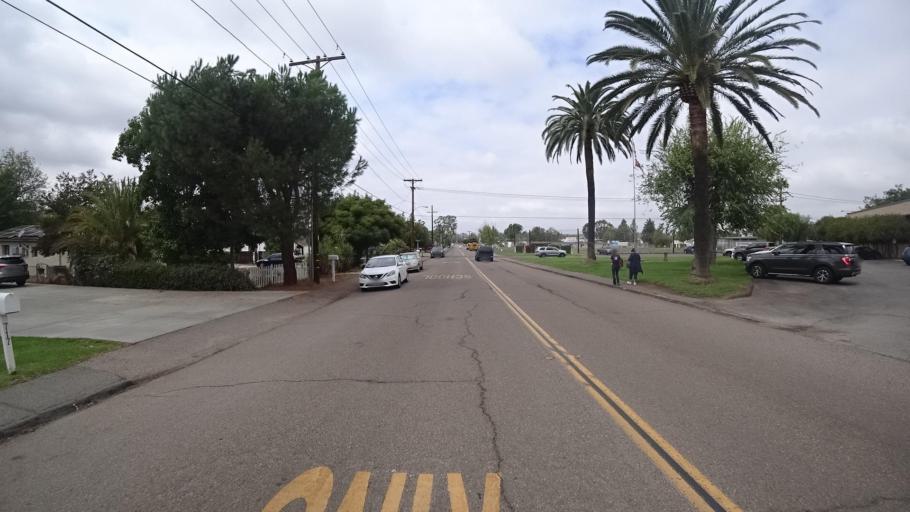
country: US
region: California
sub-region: San Diego County
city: Ramona
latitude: 33.0390
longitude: -116.8640
